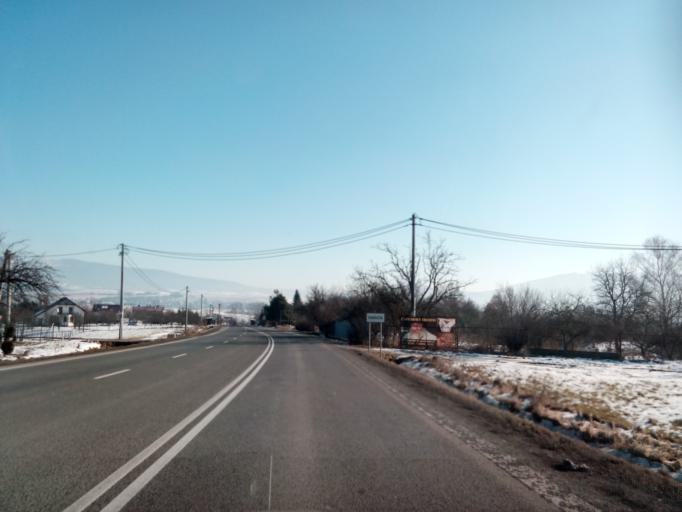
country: SK
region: Kosicky
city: Kosice
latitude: 48.7347
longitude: 21.4117
